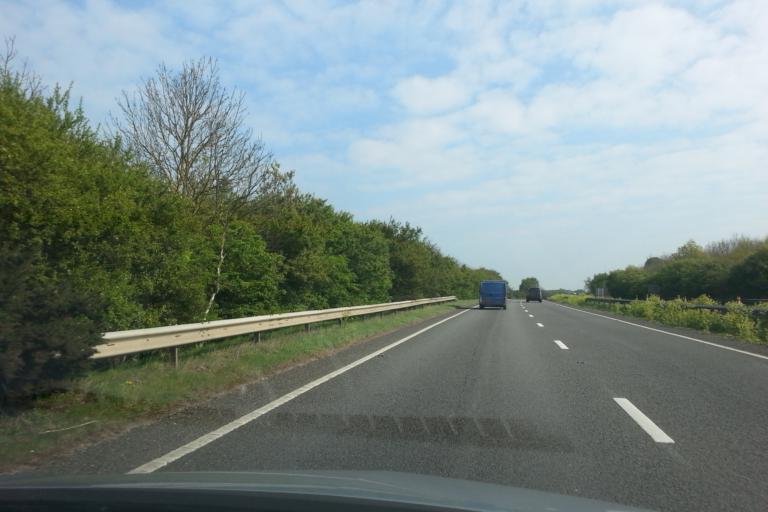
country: GB
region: England
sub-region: Suffolk
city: Kesgrave
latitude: 52.0373
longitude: 1.2602
